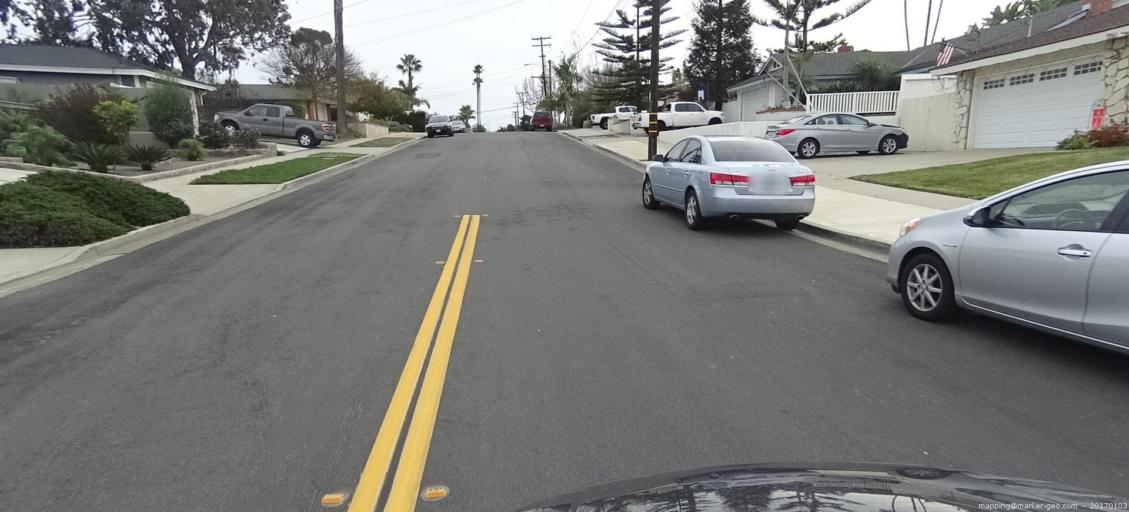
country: US
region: California
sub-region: Orange County
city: Dana Point
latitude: 33.4756
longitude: -117.6890
